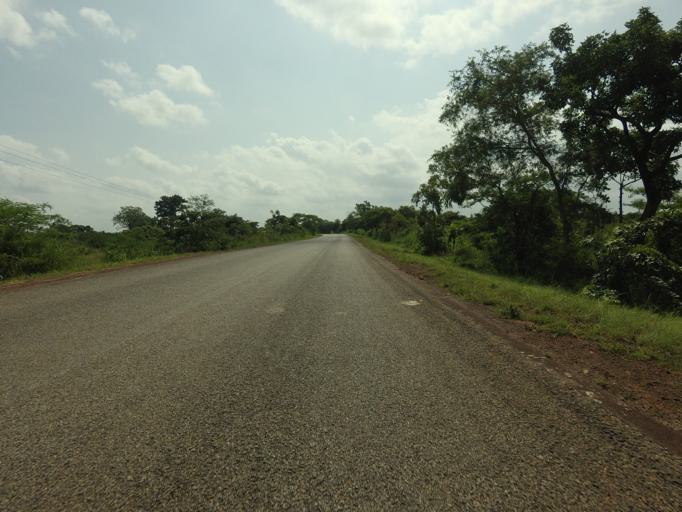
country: GH
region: Volta
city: Ho
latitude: 6.3935
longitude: 0.8108
